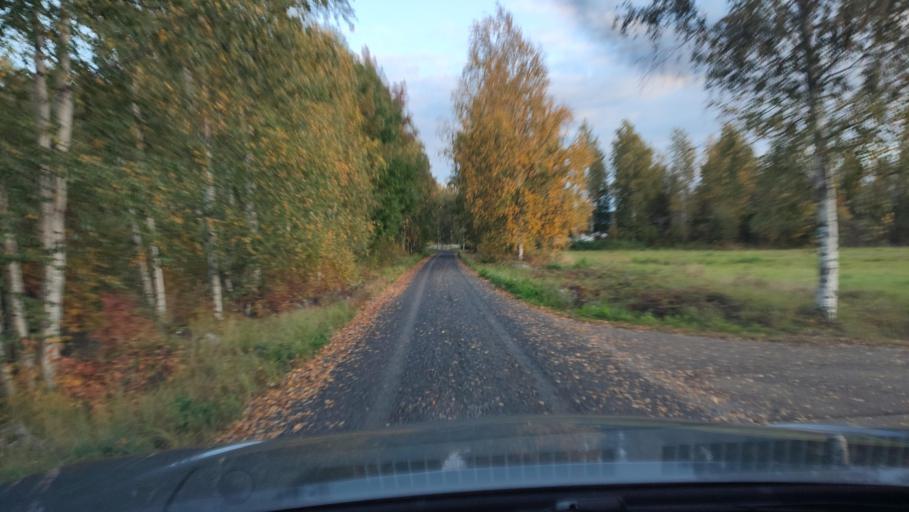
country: FI
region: Ostrobothnia
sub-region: Sydosterbotten
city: Kristinestad
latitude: 62.2473
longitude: 21.5136
